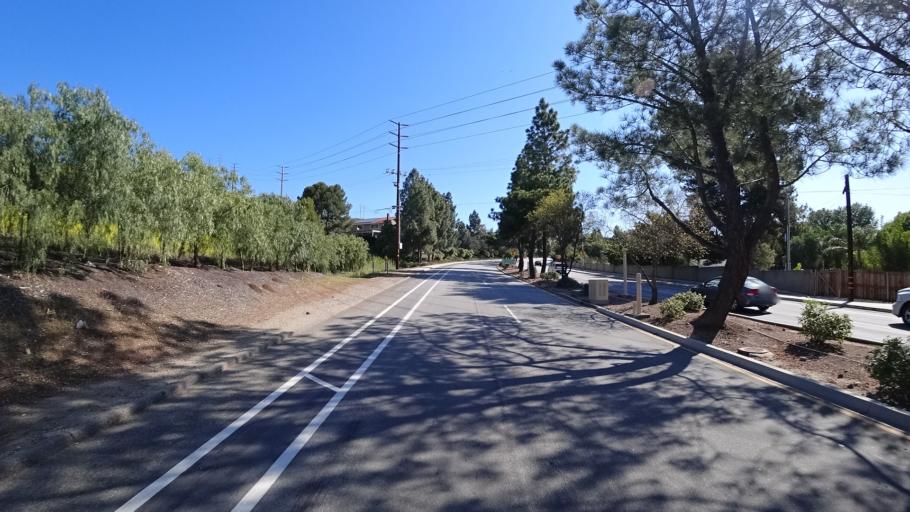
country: US
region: California
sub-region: Ventura County
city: Moorpark
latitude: 34.2288
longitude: -118.8687
